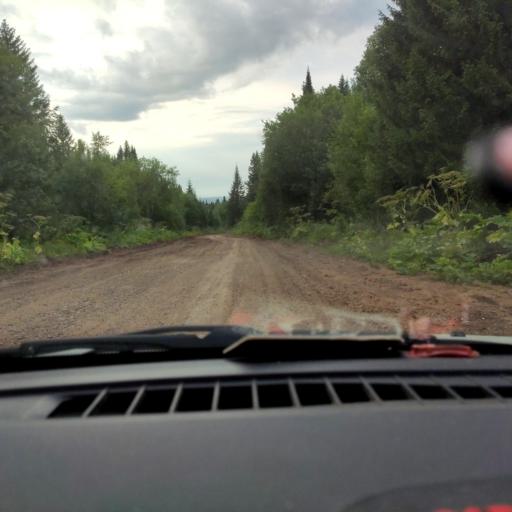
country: RU
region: Perm
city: Kultayevo
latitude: 57.8129
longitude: 56.0028
